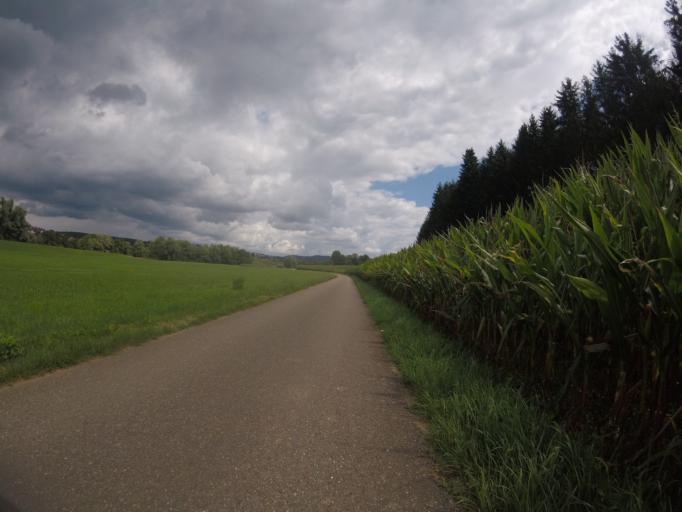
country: DE
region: Baden-Wuerttemberg
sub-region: Regierungsbezirk Stuttgart
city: Lorch
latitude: 48.7918
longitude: 9.6569
